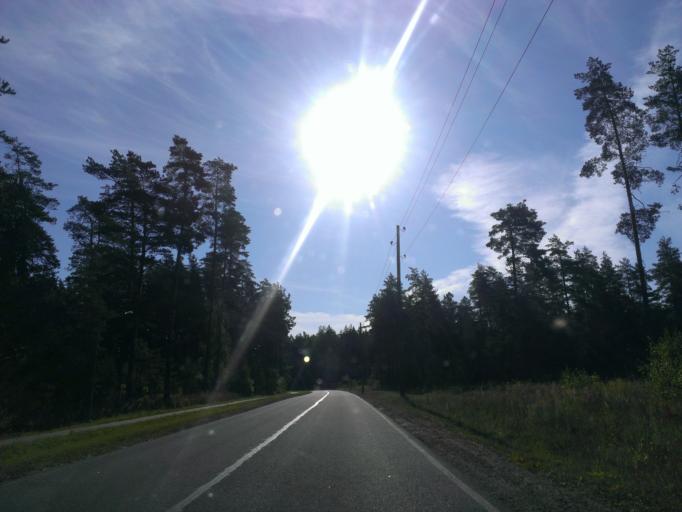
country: LV
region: Riga
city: Bergi
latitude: 56.9861
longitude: 24.3127
